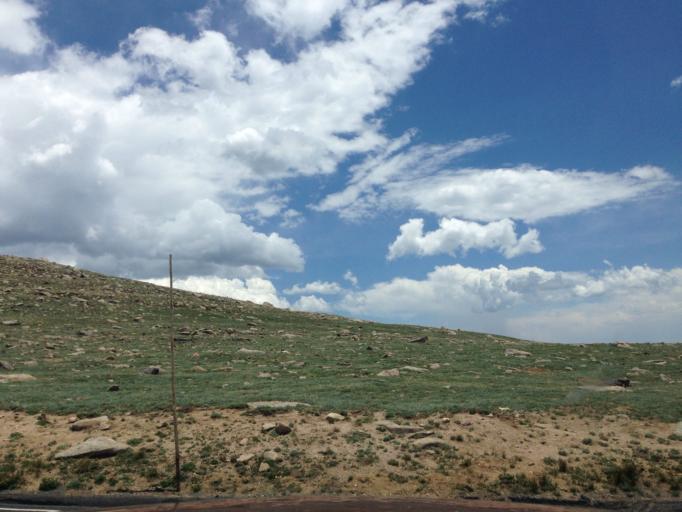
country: US
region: Colorado
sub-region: Larimer County
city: Estes Park
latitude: 40.3954
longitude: -105.7112
